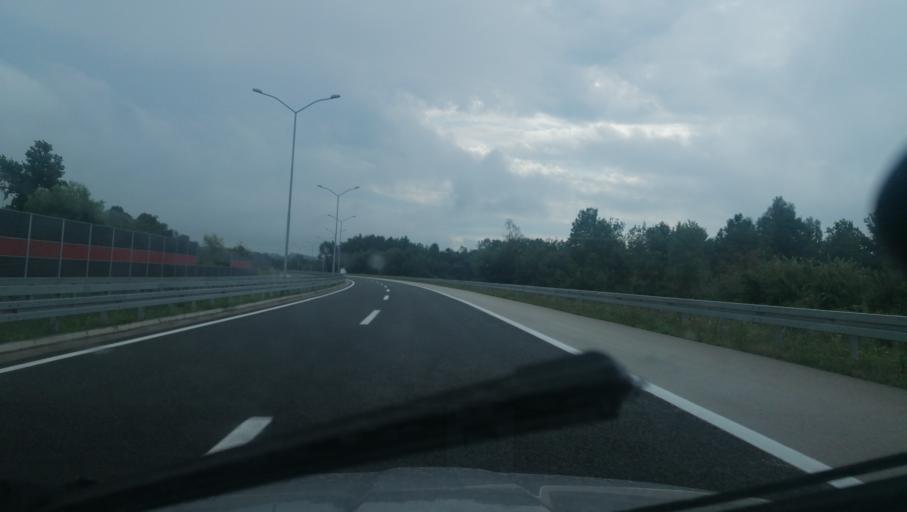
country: BA
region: Republika Srpska
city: Maglajani
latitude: 44.8996
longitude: 17.3526
